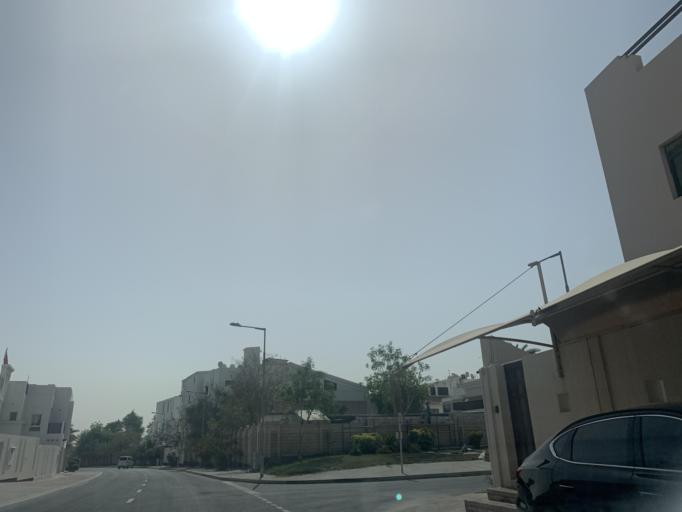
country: BH
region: Northern
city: Madinat `Isa
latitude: 26.1503
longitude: 50.5328
